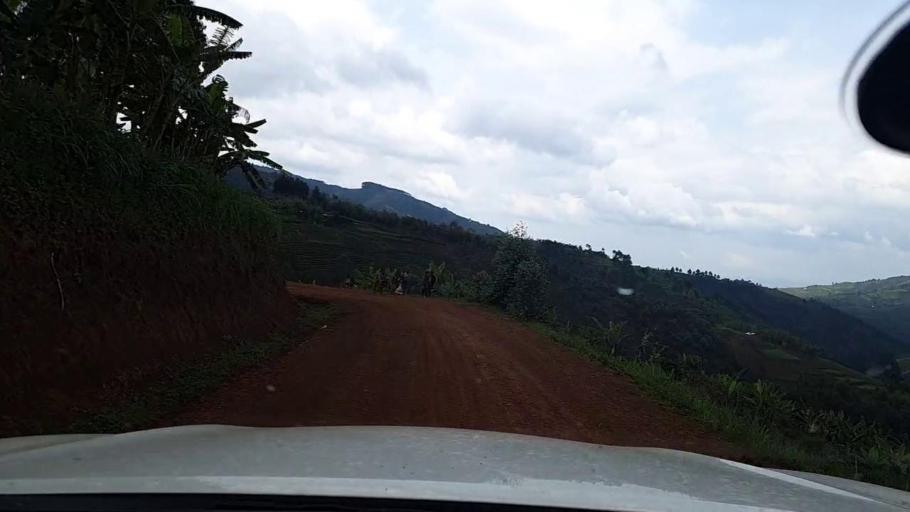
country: RW
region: Western Province
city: Kibuye
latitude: -2.1708
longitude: 29.4367
